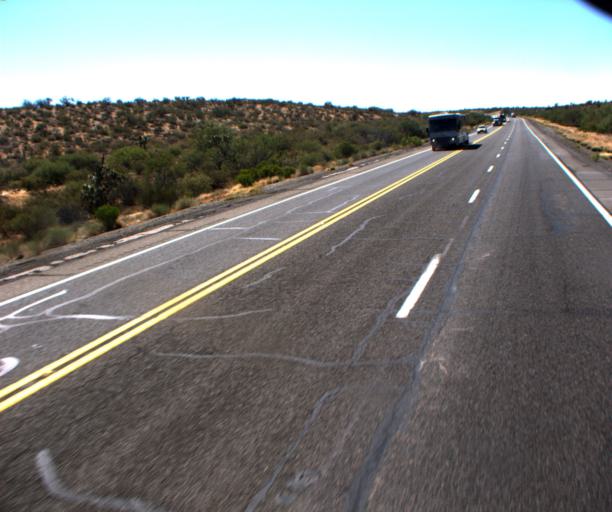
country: US
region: Arizona
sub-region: Yavapai County
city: Congress
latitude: 34.2020
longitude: -113.0624
